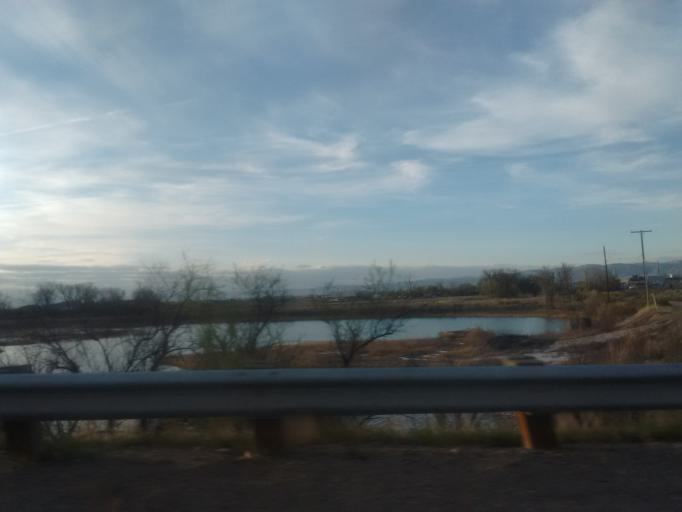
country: US
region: Colorado
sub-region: Mesa County
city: Redlands
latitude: 39.0900
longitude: -108.6223
